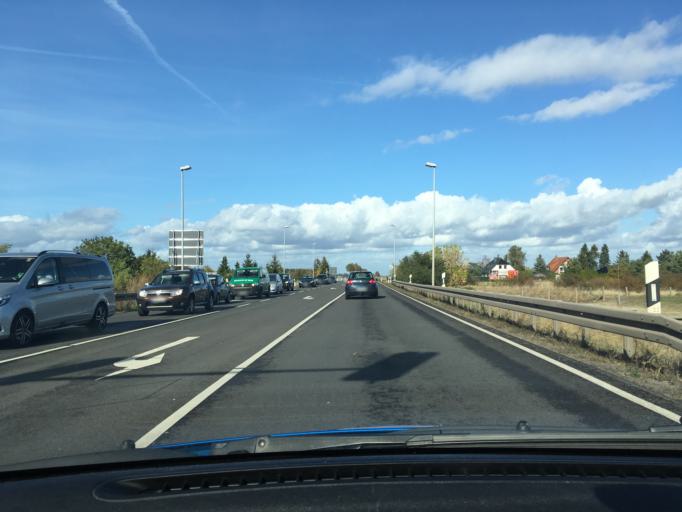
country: DE
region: Saxony-Anhalt
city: Seehausen
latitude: 52.8888
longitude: 11.7308
